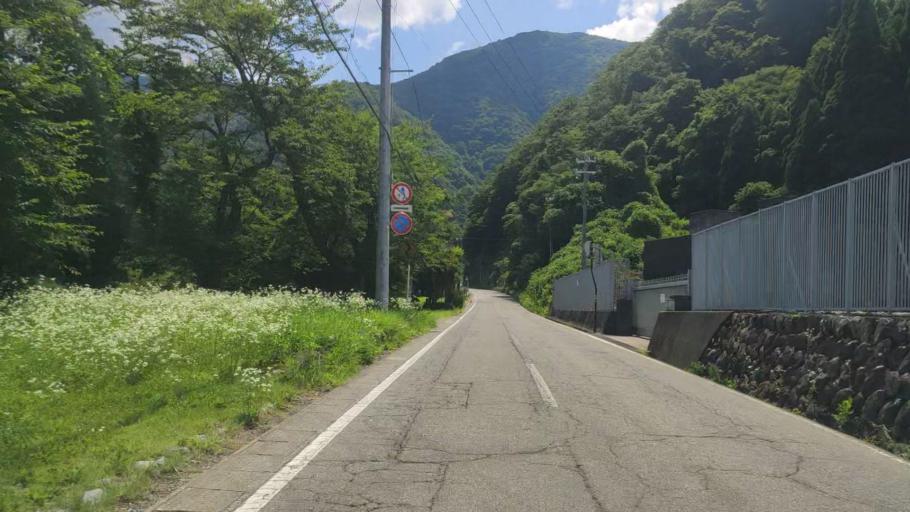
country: JP
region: Fukui
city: Ono
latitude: 35.9357
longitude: 136.5556
